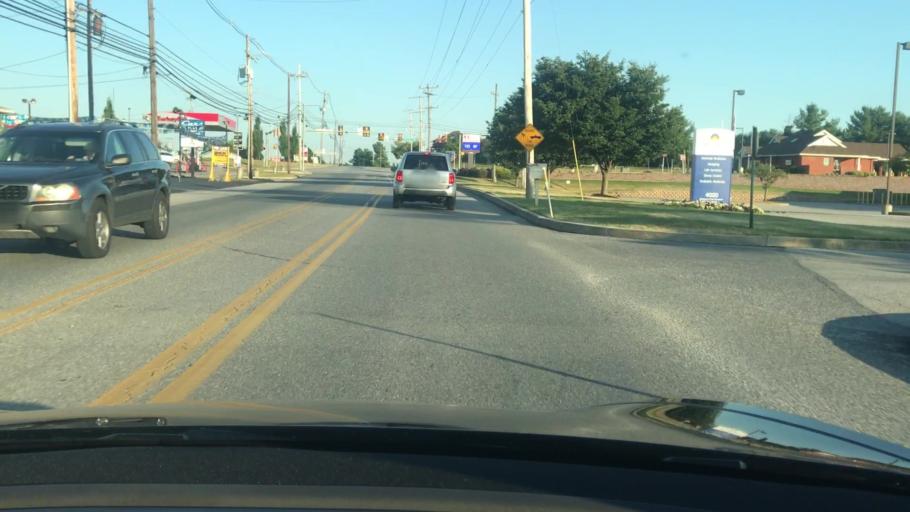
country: US
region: Pennsylvania
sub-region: York County
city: Dover
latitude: 39.9942
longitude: -76.8434
